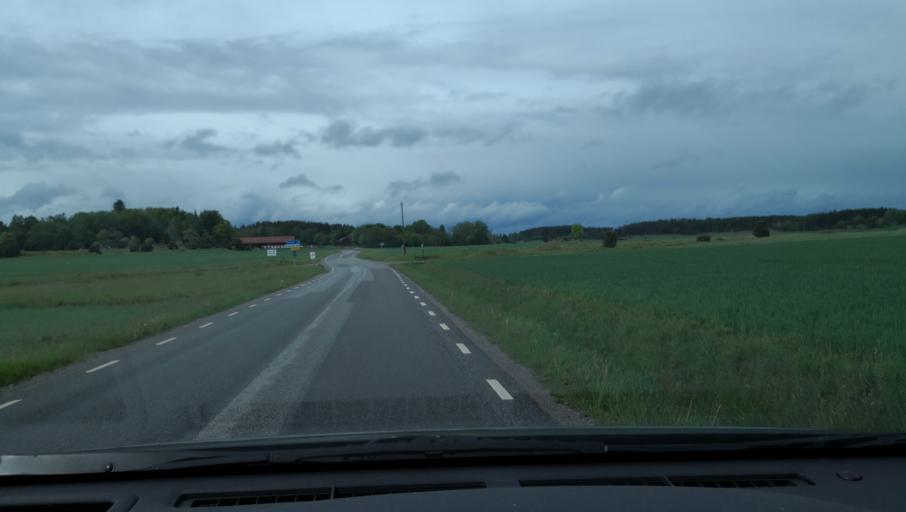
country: SE
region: Uppsala
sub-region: Enkopings Kommun
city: Orsundsbro
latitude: 59.7040
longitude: 17.3606
